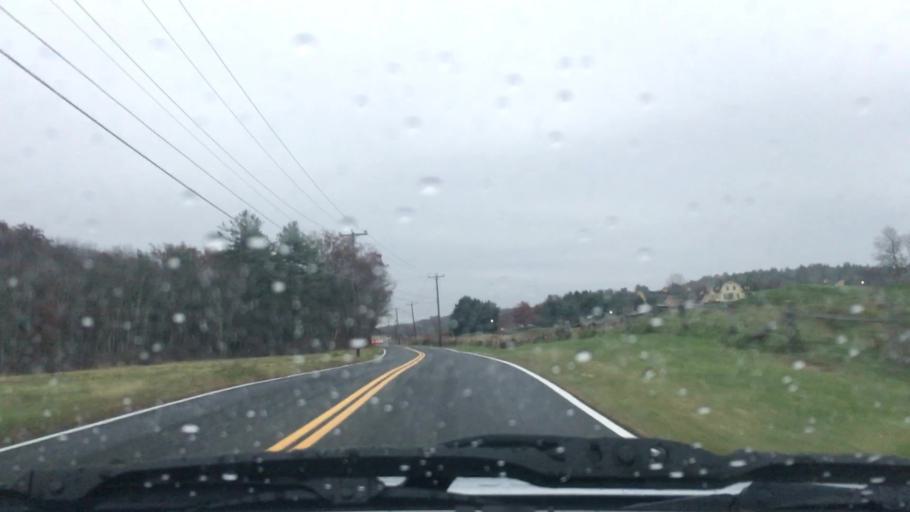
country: US
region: Massachusetts
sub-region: Hampden County
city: Southwick
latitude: 42.0886
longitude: -72.7758
